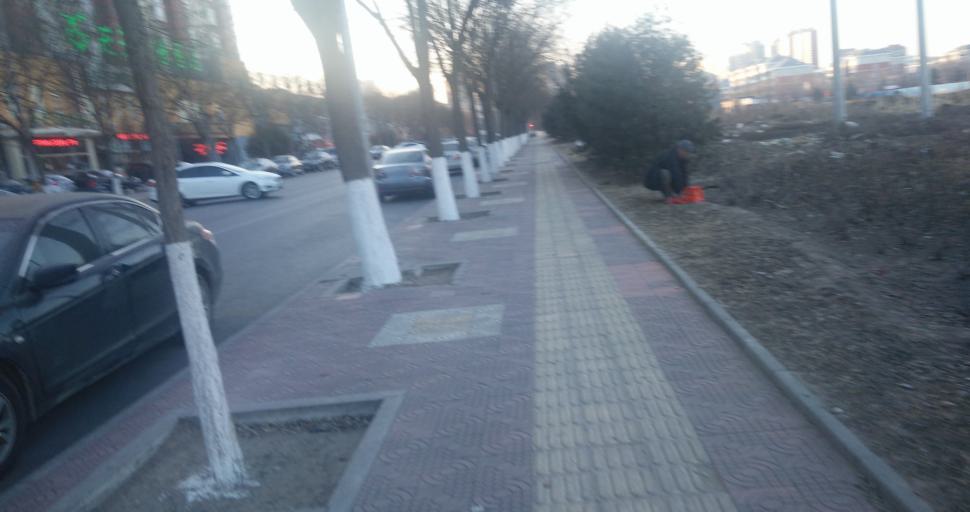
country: CN
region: Beijing
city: Yinghai
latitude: 39.7584
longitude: 116.4992
